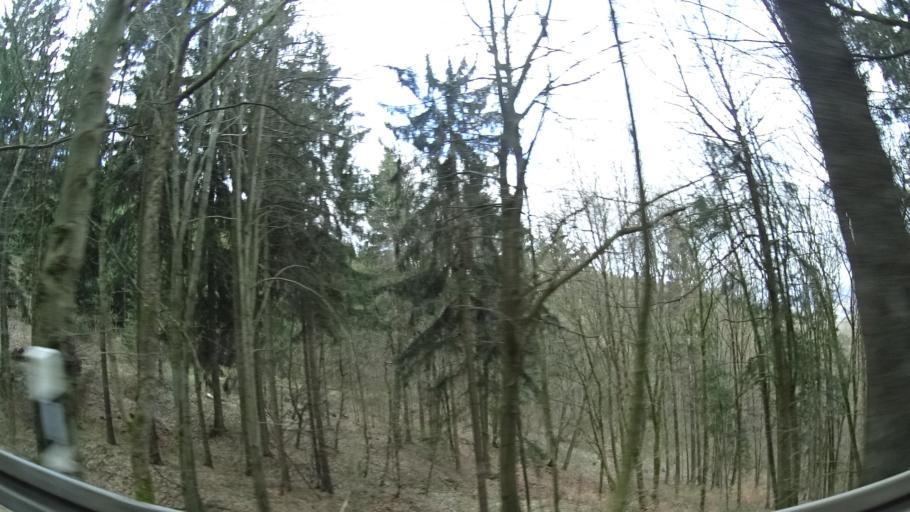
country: DE
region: Thuringia
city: Trusetal
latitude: 50.7718
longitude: 10.4456
